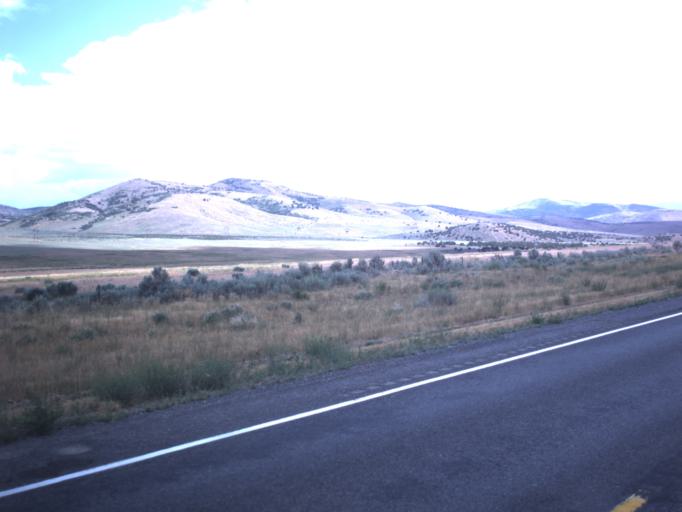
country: US
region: Utah
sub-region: Sanpete County
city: Fountain Green
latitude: 39.6778
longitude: -111.6694
